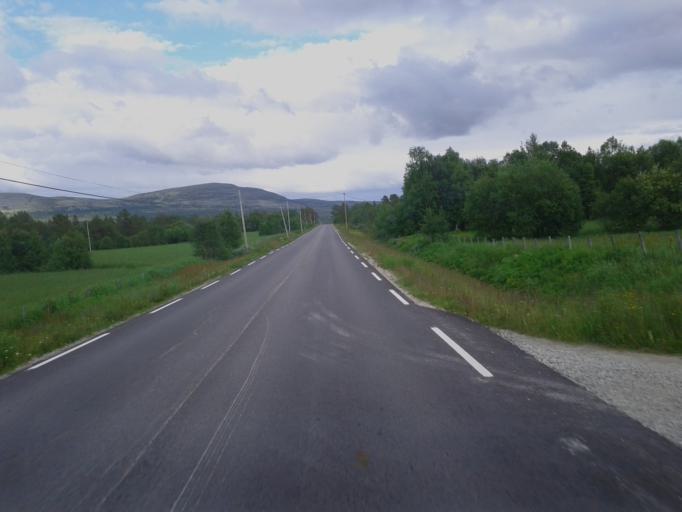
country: NO
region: Sor-Trondelag
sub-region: Roros
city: Roros
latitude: 62.3065
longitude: 11.6965
